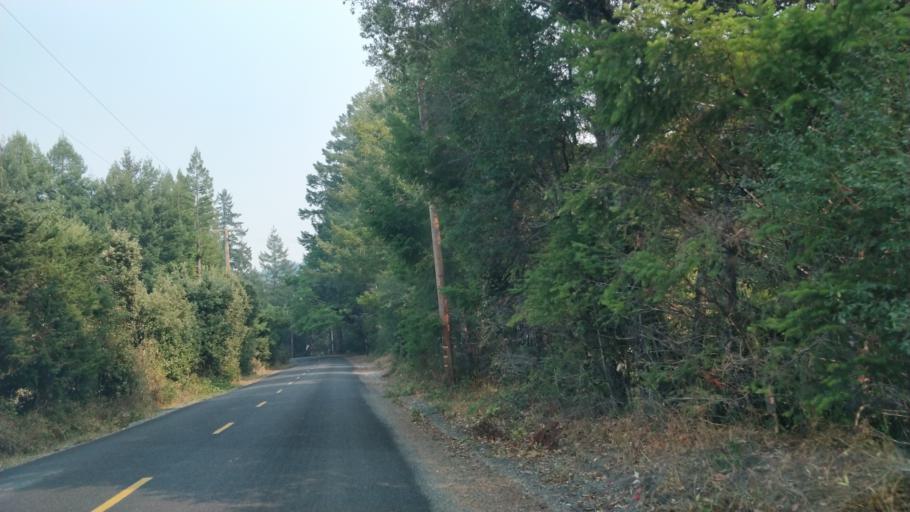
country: US
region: California
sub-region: Humboldt County
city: Rio Dell
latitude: 40.2690
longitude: -124.2249
